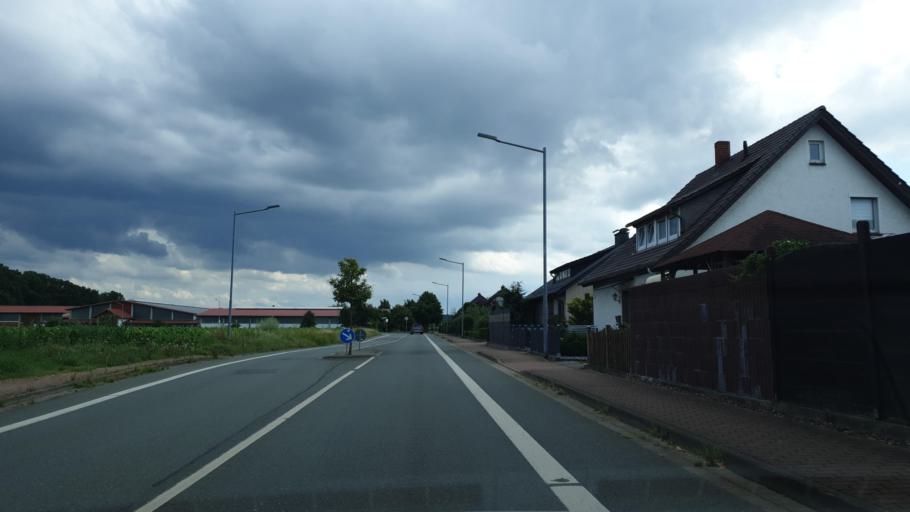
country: DE
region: North Rhine-Westphalia
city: Loehne
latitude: 52.2115
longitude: 8.7422
